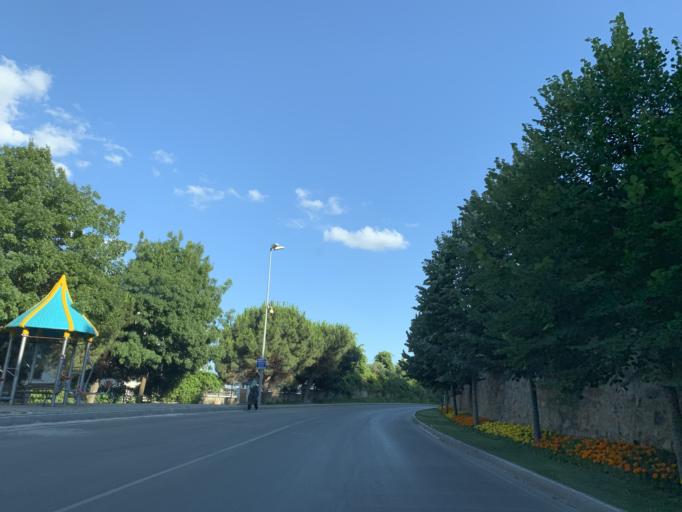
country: TR
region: Istanbul
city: Pendik
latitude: 40.8913
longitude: 29.2548
